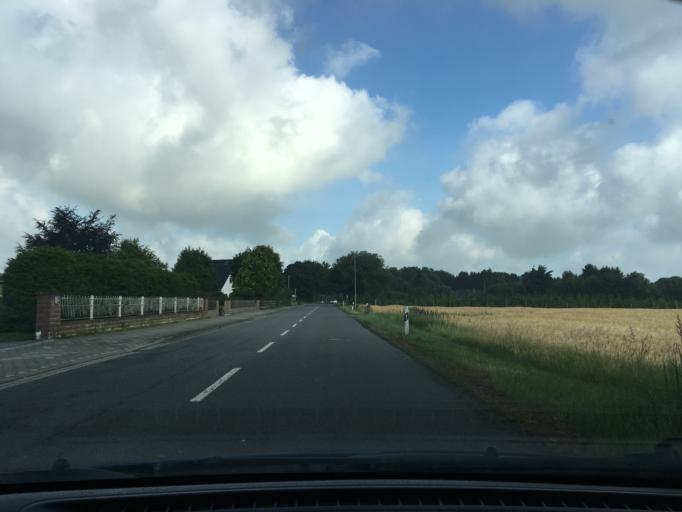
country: DE
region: Lower Saxony
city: Buchholz in der Nordheide
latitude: 53.3277
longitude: 9.8378
